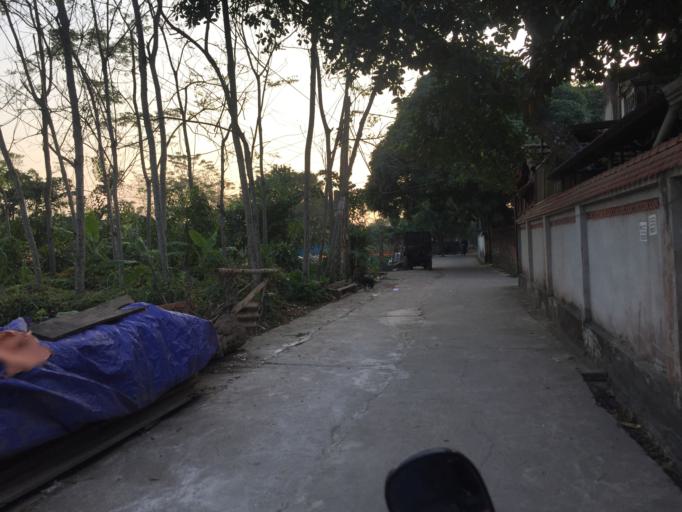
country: VN
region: Ha Noi
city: Chuc Son
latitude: 20.9086
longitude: 105.7300
